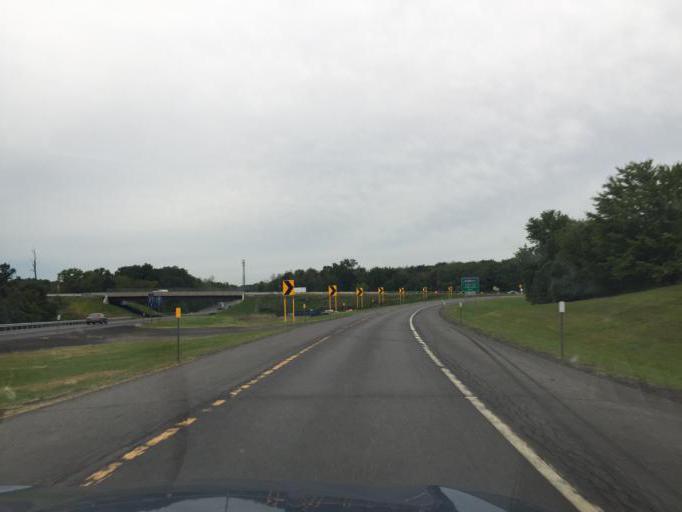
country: US
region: New York
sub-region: Columbia County
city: Niverville
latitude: 42.4827
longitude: -73.6675
